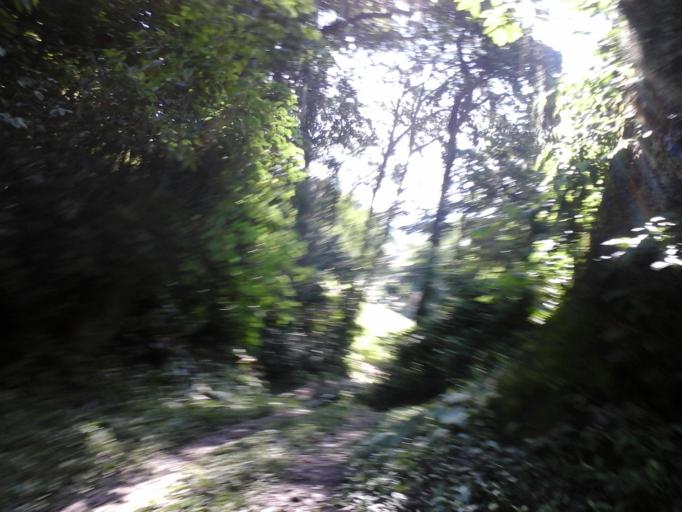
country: CO
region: Cesar
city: Agustin Codazzi
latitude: 9.9474
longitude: -73.0897
